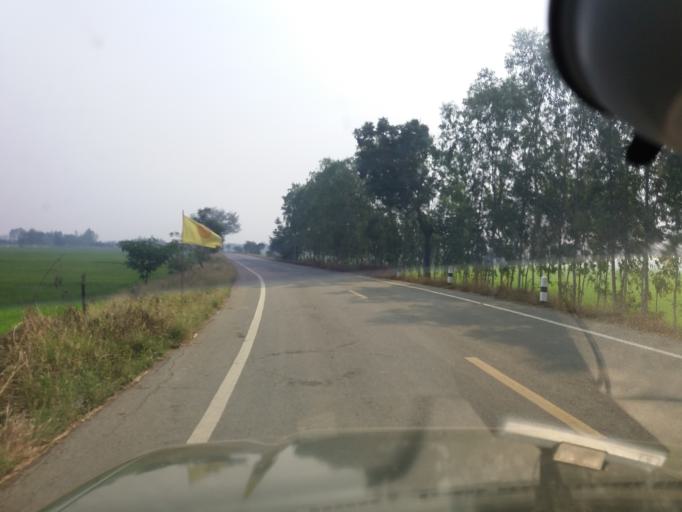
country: TH
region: Suphan Buri
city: Doem Bang Nang Buat
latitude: 14.8554
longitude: 100.1548
